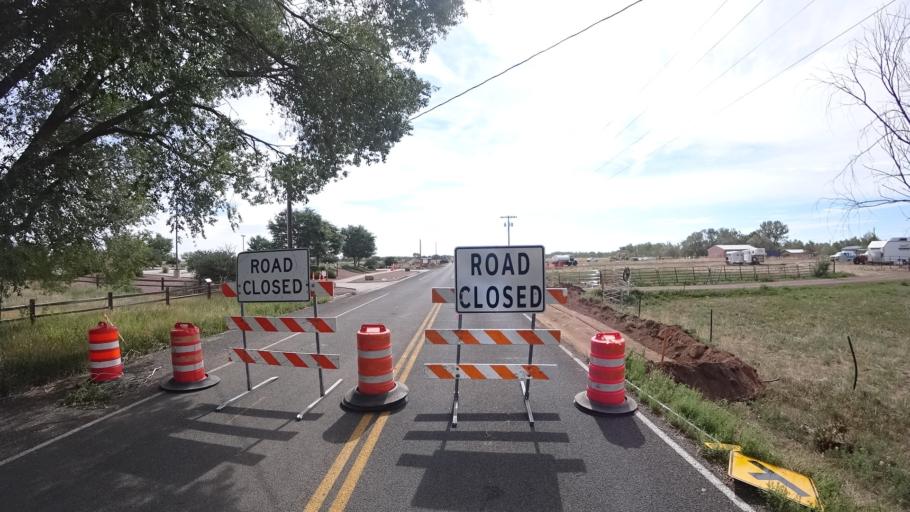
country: US
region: Colorado
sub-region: El Paso County
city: Fountain
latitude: 38.7084
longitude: -104.6755
